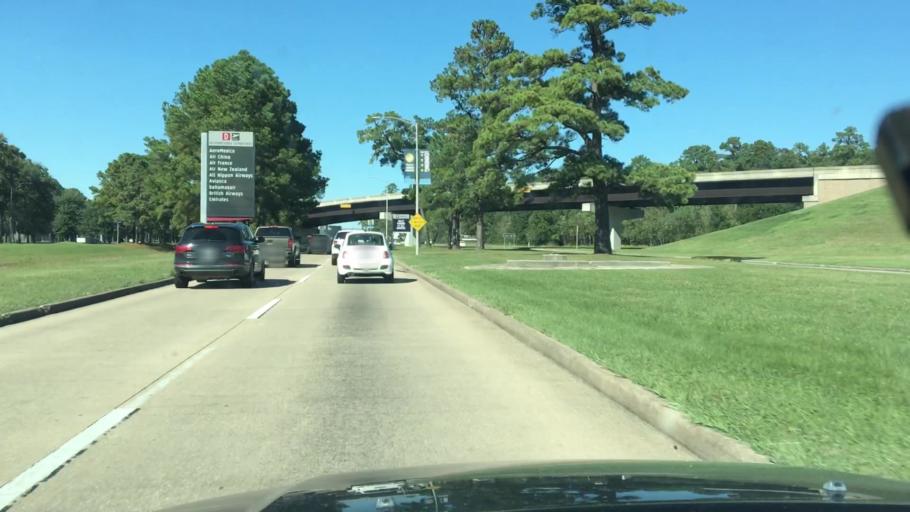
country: US
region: Texas
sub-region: Harris County
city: Aldine
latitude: 29.9688
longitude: -95.3379
